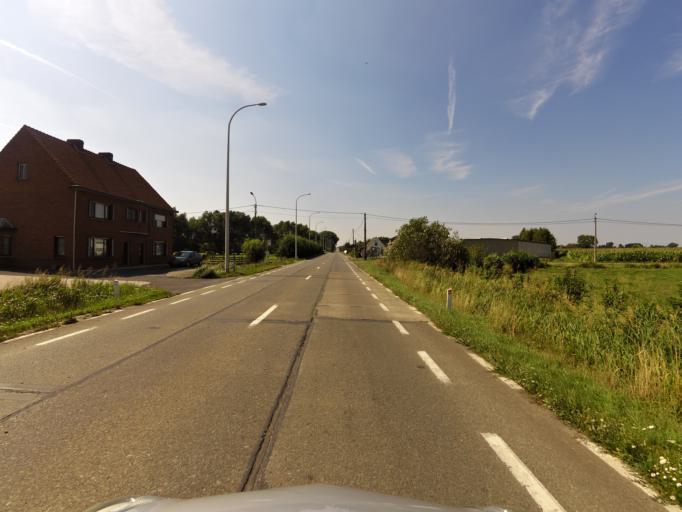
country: BE
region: Flanders
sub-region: Provincie West-Vlaanderen
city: Dentergem
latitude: 50.9894
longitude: 3.4502
